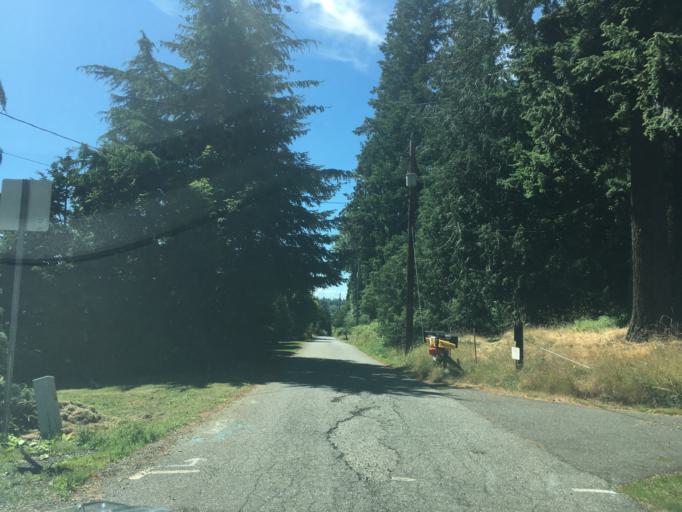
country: US
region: Washington
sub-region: Whatcom County
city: Geneva
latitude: 48.7604
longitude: -122.3950
